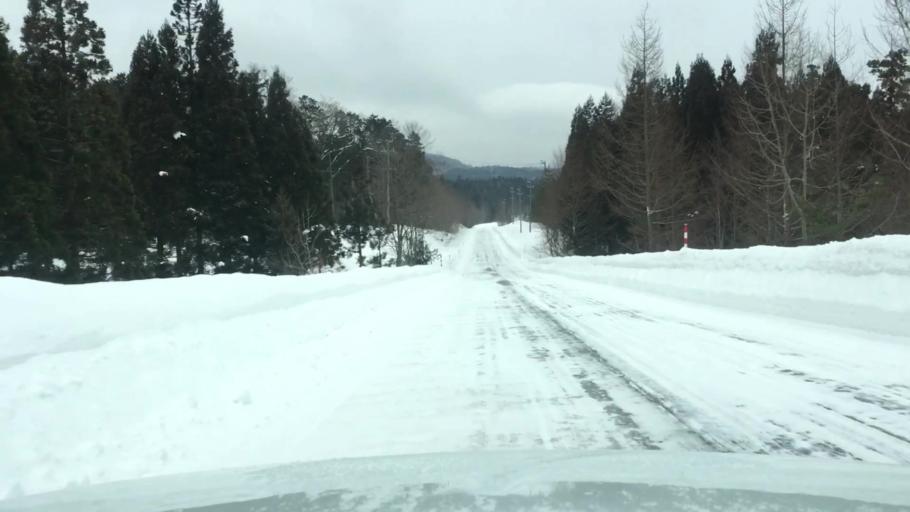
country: JP
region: Akita
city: Hanawa
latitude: 39.9862
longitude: 141.0011
